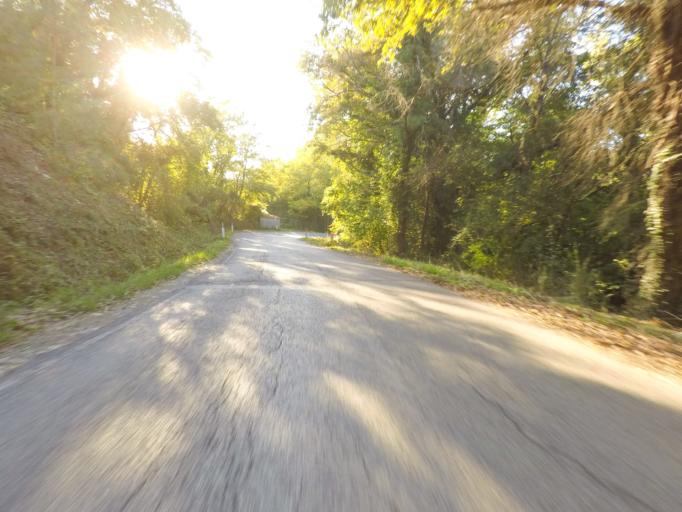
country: IT
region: Tuscany
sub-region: Provincia di Siena
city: Radda in Chianti
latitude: 43.4673
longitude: 11.3738
